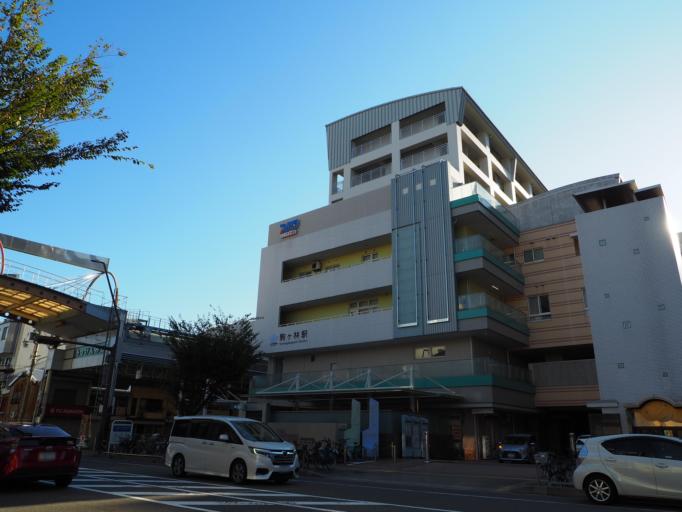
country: JP
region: Hyogo
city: Kobe
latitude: 34.6530
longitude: 135.1489
